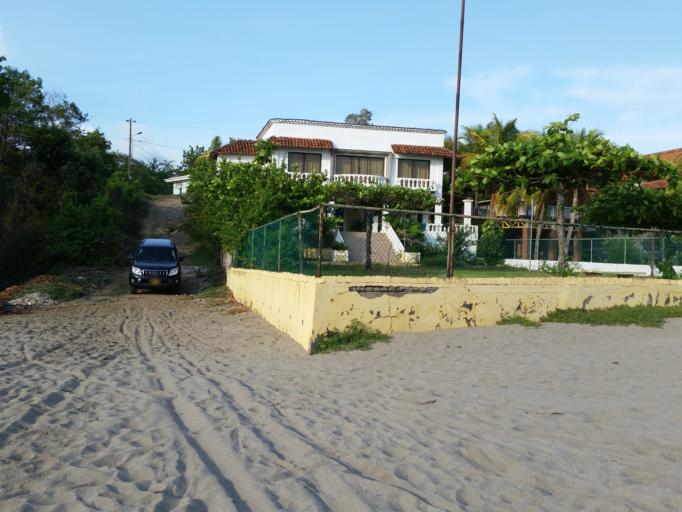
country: NI
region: Managua
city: Masachapa
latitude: 11.7640
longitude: -86.4982
